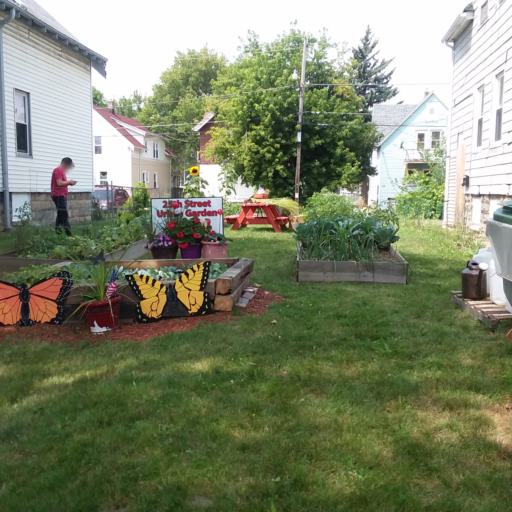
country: US
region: Wisconsin
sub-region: Milwaukee County
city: Glendale
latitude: 43.0831
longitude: -87.9450
